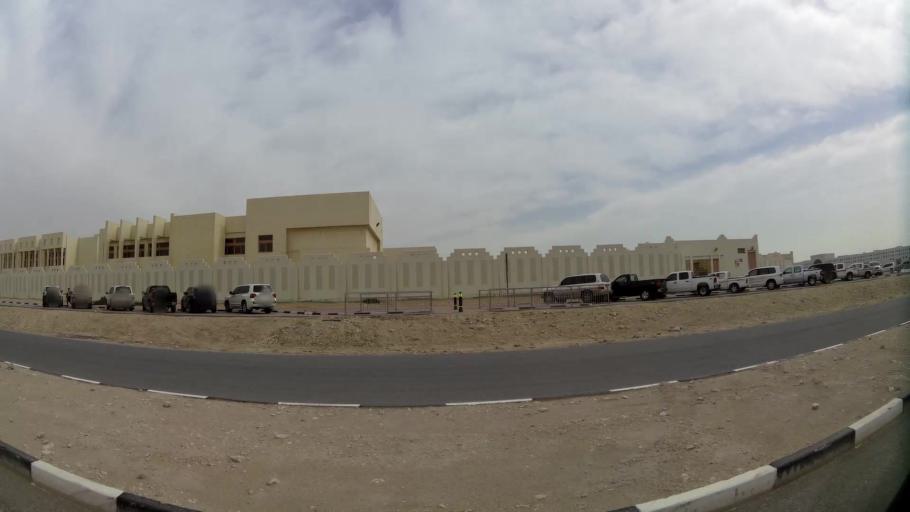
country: QA
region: Baladiyat ad Dawhah
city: Doha
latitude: 25.2152
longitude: 51.4932
